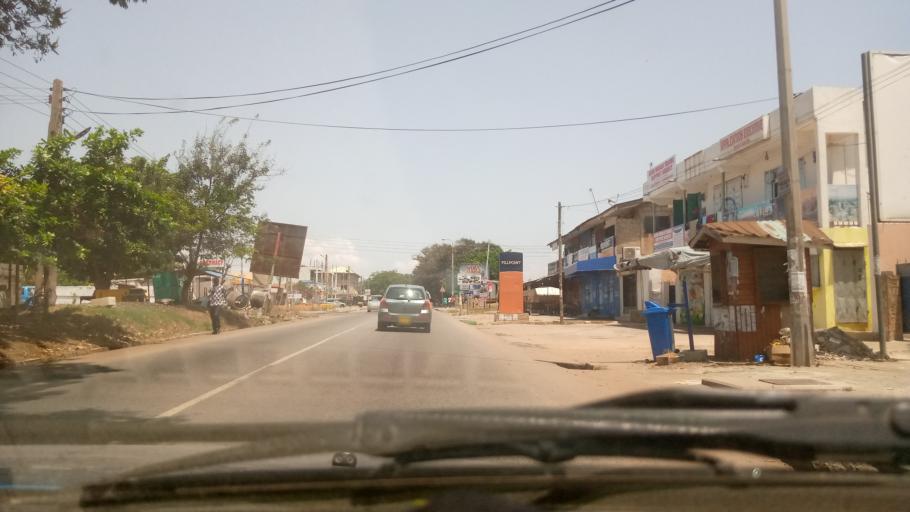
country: GH
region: Greater Accra
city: Accra
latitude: 5.5400
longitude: -0.2390
